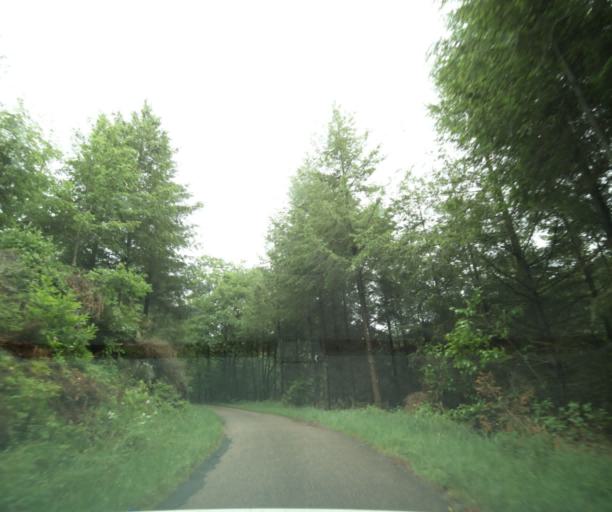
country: FR
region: Bourgogne
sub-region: Departement de Saone-et-Loire
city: Matour
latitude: 46.4469
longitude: 4.4675
